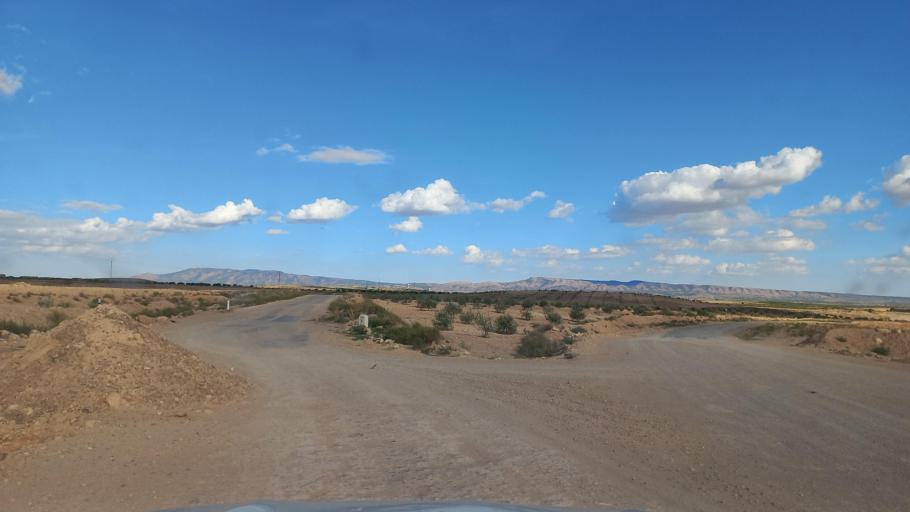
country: TN
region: Al Qasrayn
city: Sbiba
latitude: 35.3924
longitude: 9.0186
